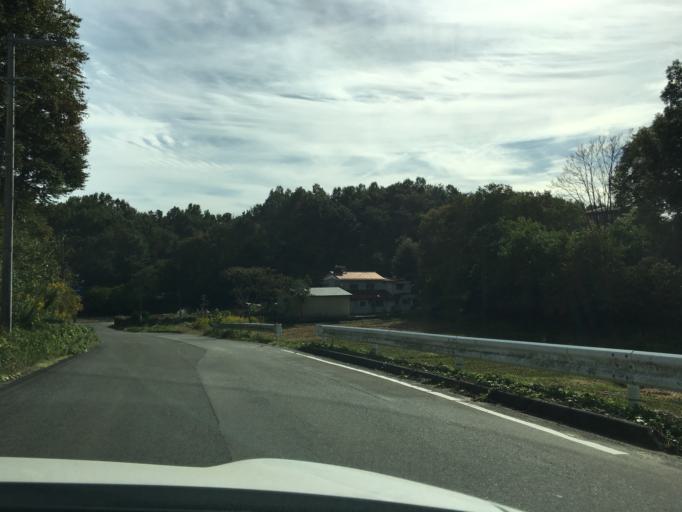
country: JP
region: Fukushima
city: Nihommatsu
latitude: 37.5684
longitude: 140.4992
